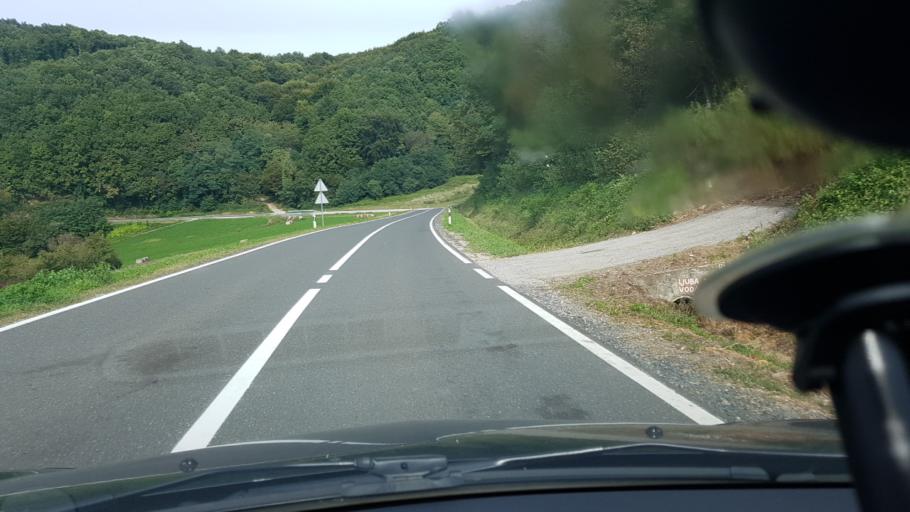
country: HR
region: Varazdinska
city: Ljubescica
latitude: 46.1185
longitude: 16.3557
